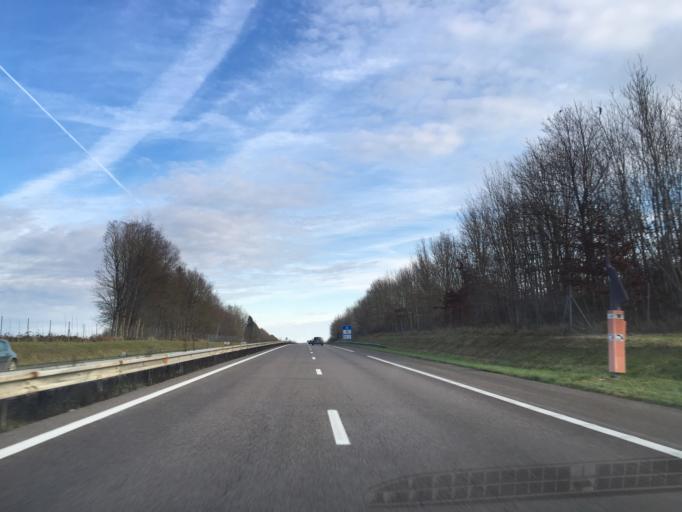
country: FR
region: Picardie
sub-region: Departement de l'Aisne
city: Chateau-Thierry
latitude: 49.0858
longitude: 3.4143
